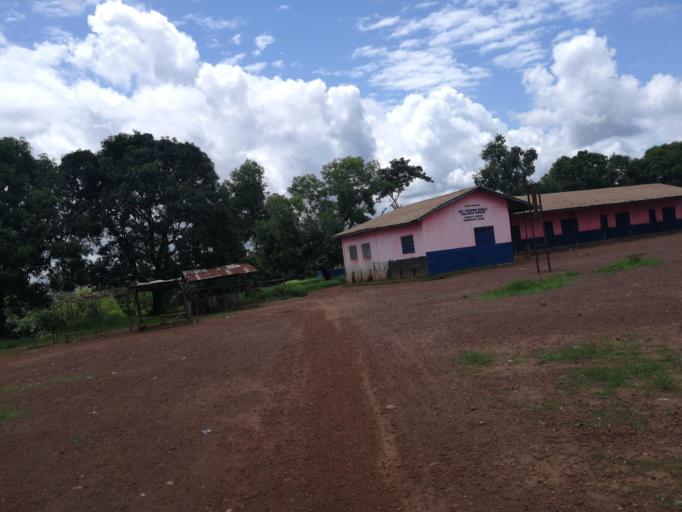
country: SL
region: Northern Province
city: Port Loko
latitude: 8.7691
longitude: -12.7811
